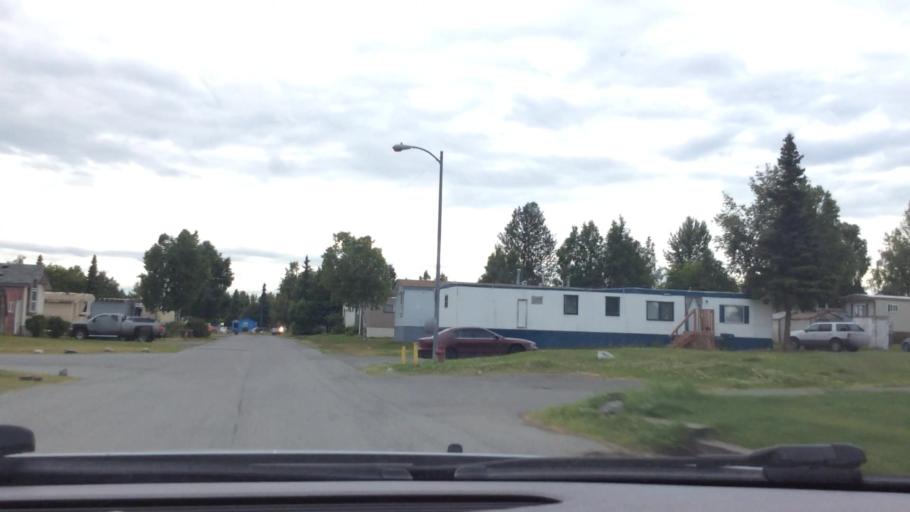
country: US
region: Alaska
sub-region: Anchorage Municipality
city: Anchorage
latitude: 61.1344
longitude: -149.8504
